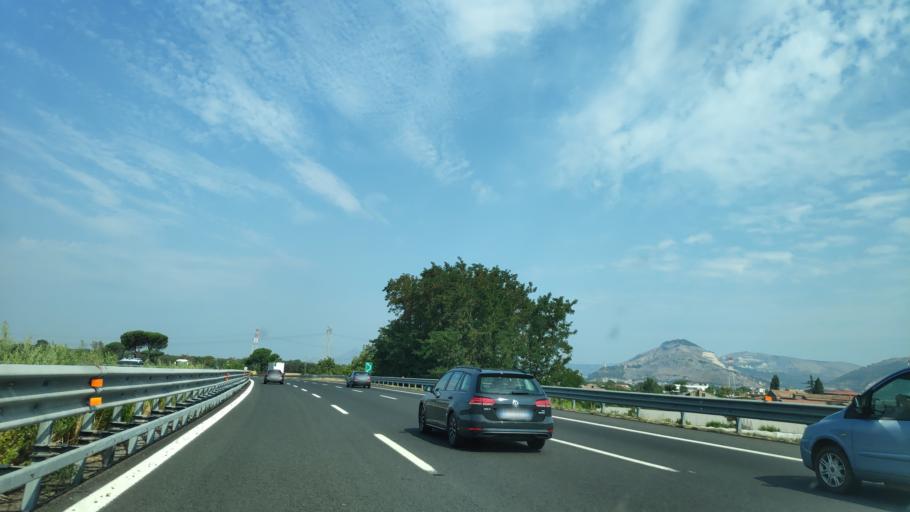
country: IT
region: Campania
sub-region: Provincia di Caserta
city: Montedecoro
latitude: 41.0069
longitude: 14.4020
